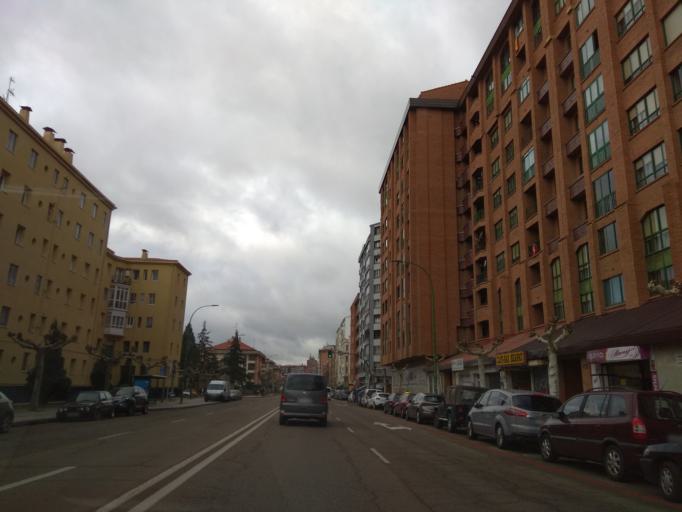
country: ES
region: Castille and Leon
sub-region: Provincia de Burgos
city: Burgos
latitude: 42.3474
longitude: -3.6798
